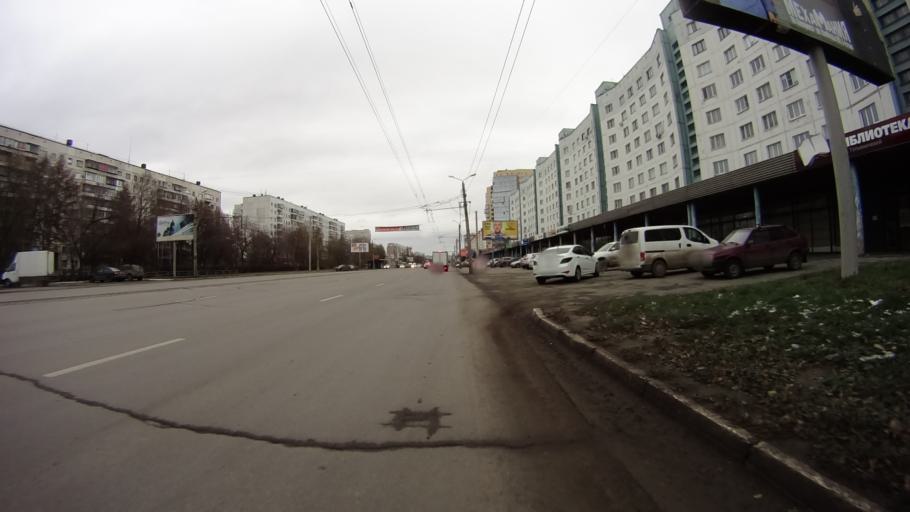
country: RU
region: Chelyabinsk
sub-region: Gorod Chelyabinsk
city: Chelyabinsk
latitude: 55.1945
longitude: 61.3377
